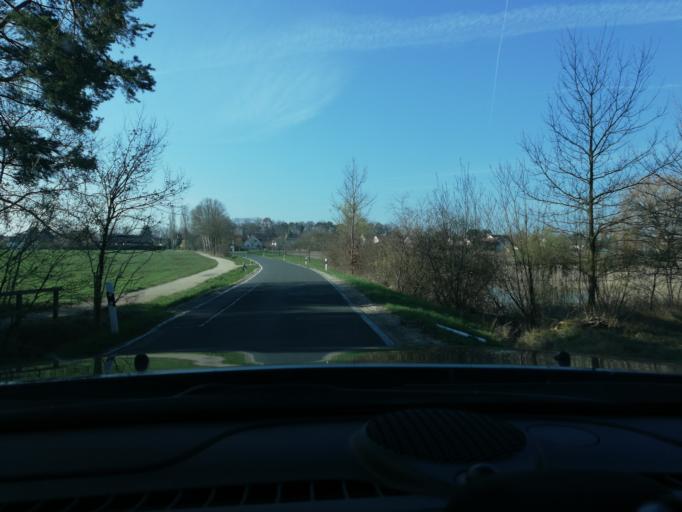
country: DE
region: Bavaria
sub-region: Regierungsbezirk Mittelfranken
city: Hessdorf
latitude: 49.6063
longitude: 10.9371
